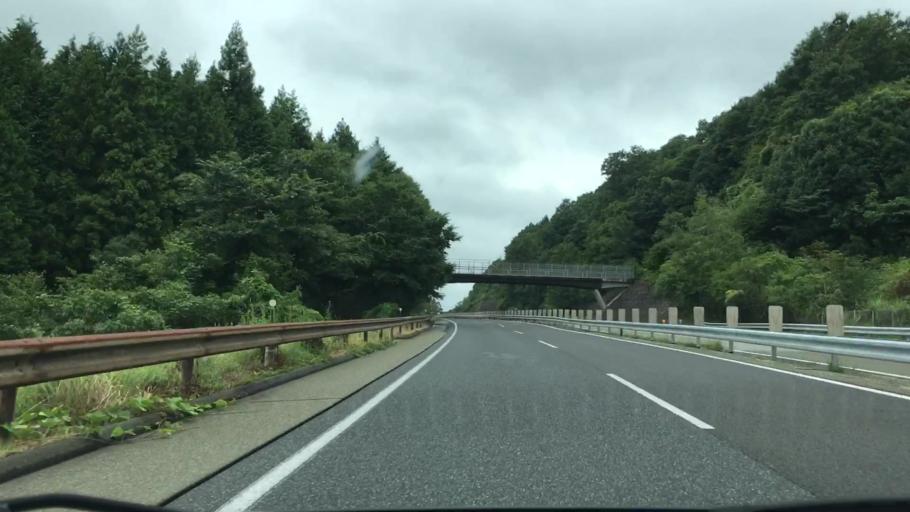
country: JP
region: Hiroshima
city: Shobara
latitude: 34.8272
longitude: 133.0568
